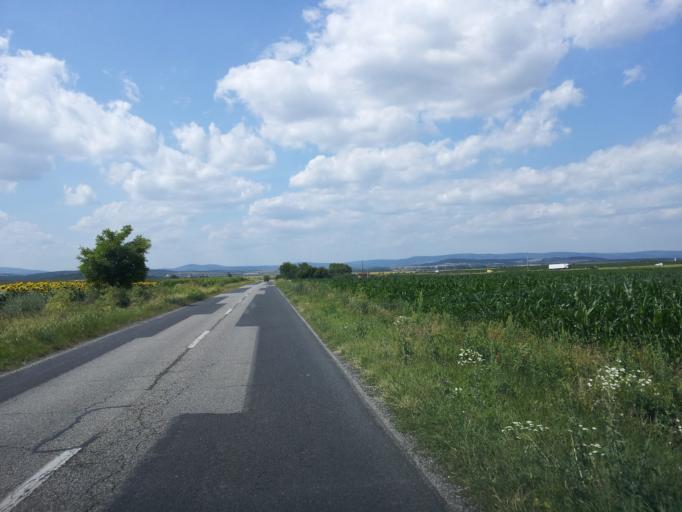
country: HU
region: Veszprem
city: Balatonkenese
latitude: 47.0630
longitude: 18.0798
